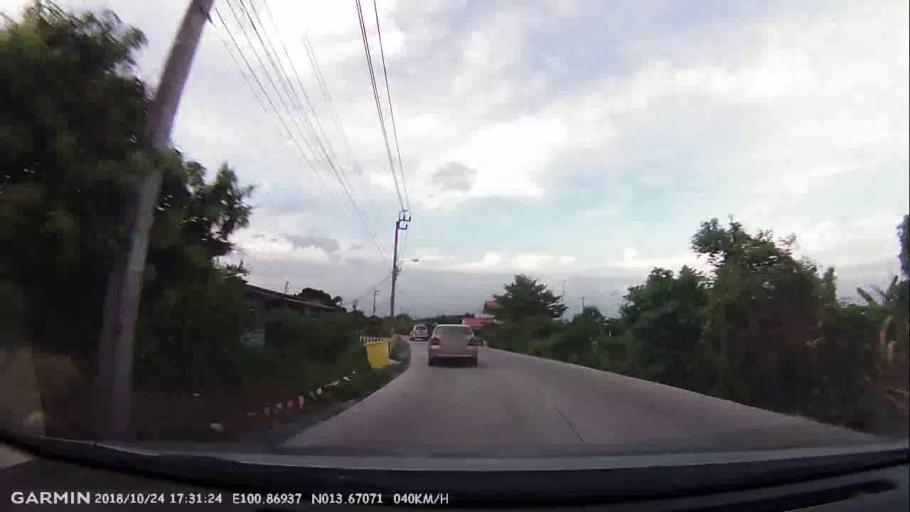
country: TH
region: Samut Prakan
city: Ban Khlong Bang Sao Thong
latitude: 13.6708
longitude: 100.8694
